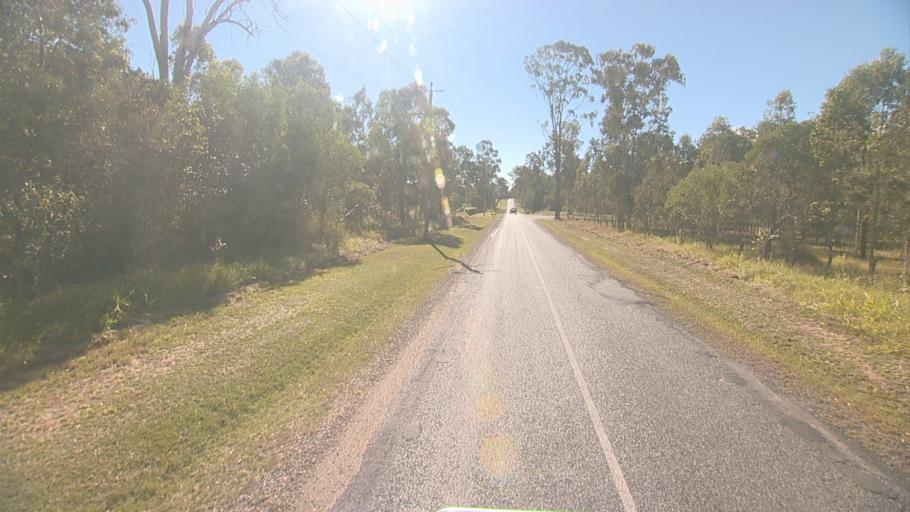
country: AU
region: Queensland
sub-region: Logan
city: Chambers Flat
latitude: -27.7997
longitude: 153.0708
